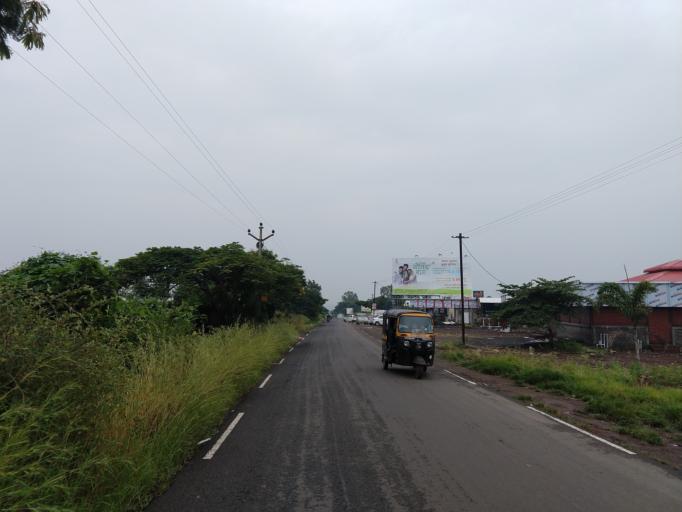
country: IN
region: Maharashtra
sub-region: Pune Division
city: Khed
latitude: 18.4031
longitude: 73.9116
